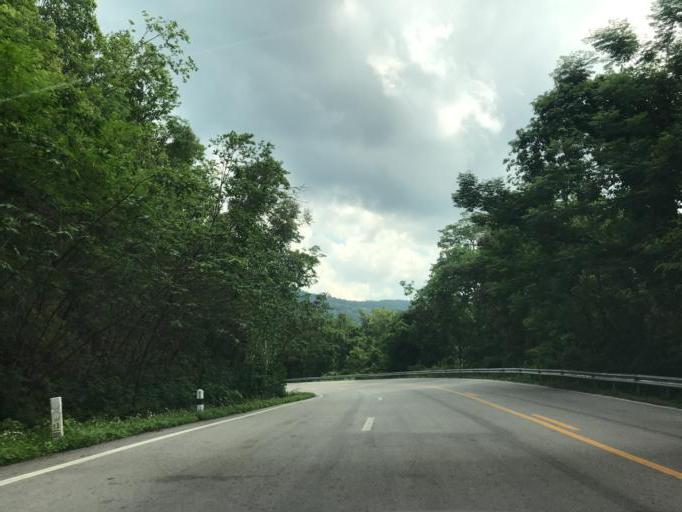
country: TH
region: Phayao
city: Phayao
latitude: 19.0820
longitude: 99.8124
